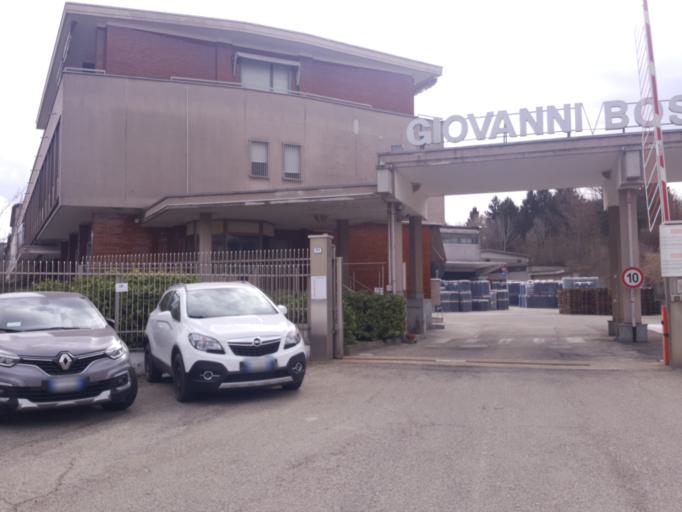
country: IT
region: Piedmont
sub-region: Provincia di Asti
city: Canelli
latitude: 44.7342
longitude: 8.2923
